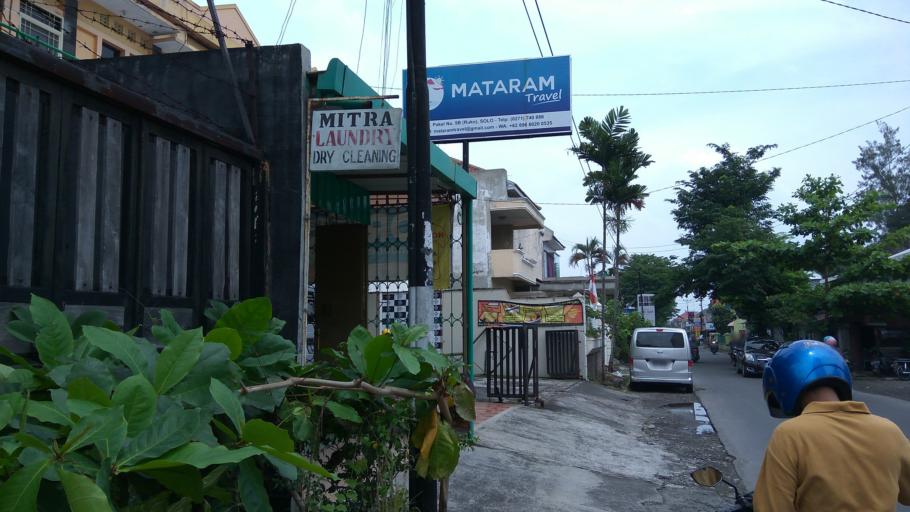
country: ID
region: Central Java
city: Surakarta
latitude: -7.5517
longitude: 110.7953
